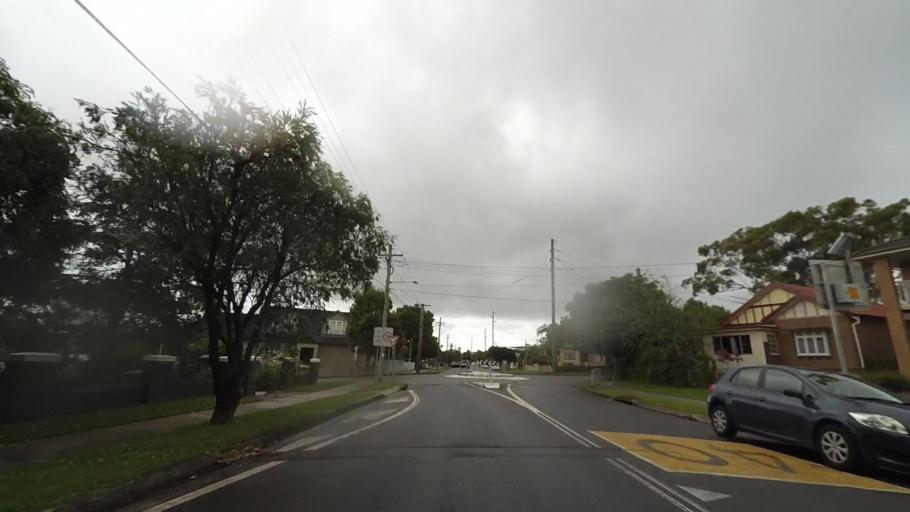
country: AU
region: New South Wales
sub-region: Kogarah
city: Kogarah Bay
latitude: -33.9919
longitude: 151.1289
